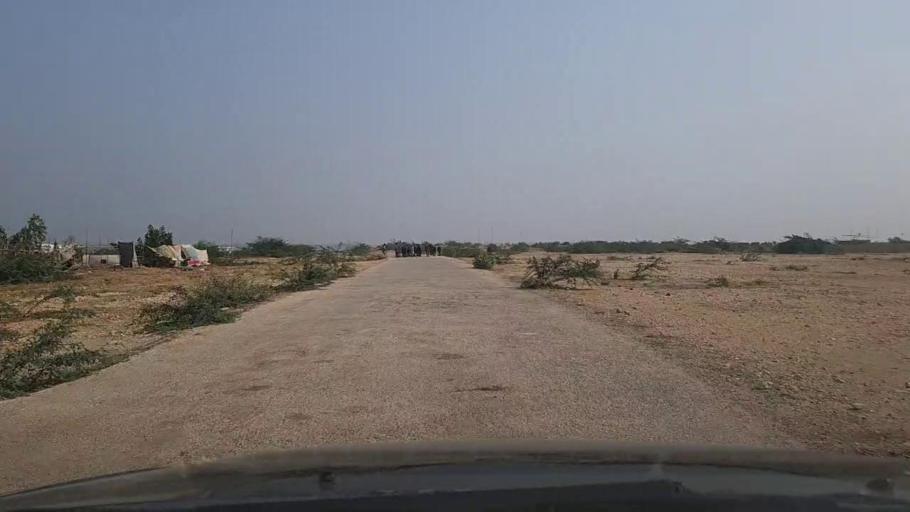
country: PK
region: Sindh
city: Thatta
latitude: 24.7445
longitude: 67.9033
